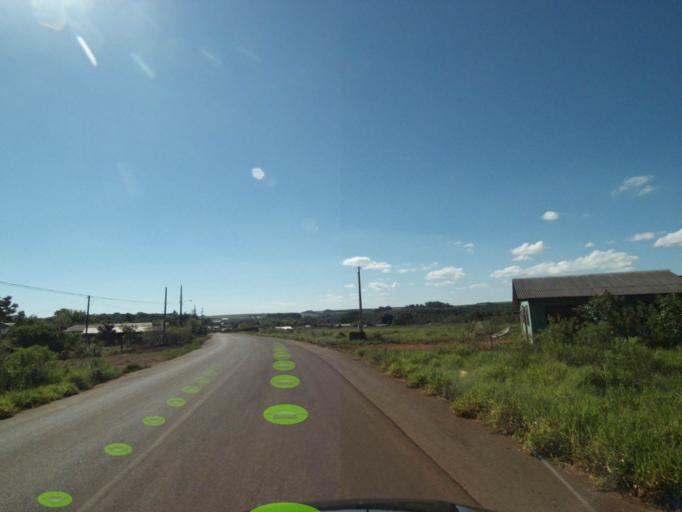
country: BR
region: Parana
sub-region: Coronel Vivida
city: Coronel Vivida
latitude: -26.1476
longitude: -52.3694
